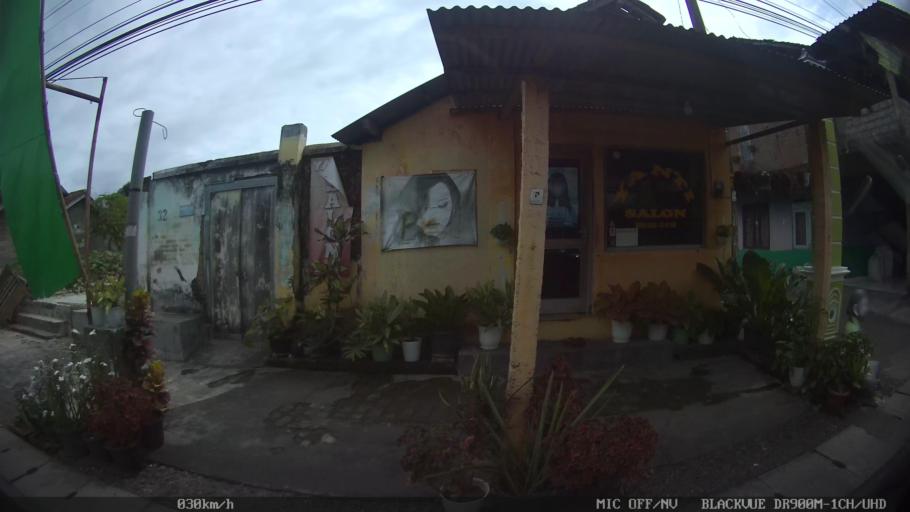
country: ID
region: Daerah Istimewa Yogyakarta
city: Depok
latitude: -7.8053
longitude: 110.4531
